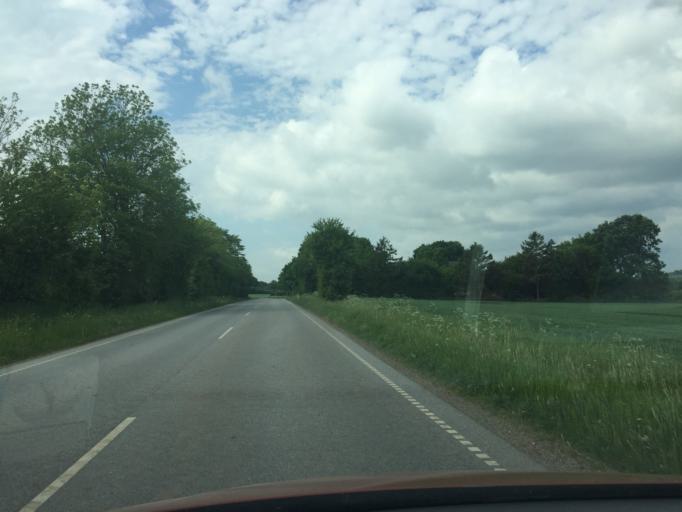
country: DK
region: South Denmark
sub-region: Haderslev Kommune
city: Starup
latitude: 55.2461
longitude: 9.5714
